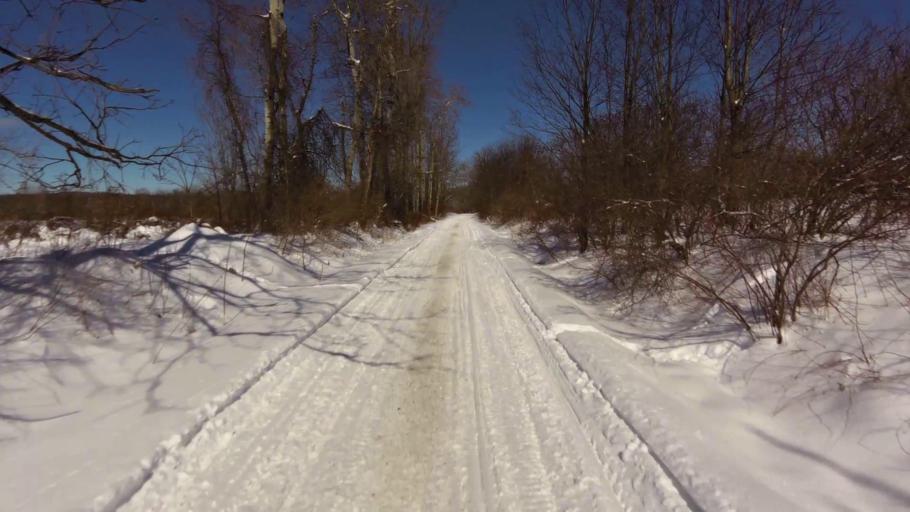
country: US
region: New York
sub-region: Chautauqua County
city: Celoron
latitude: 42.2357
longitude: -79.2693
